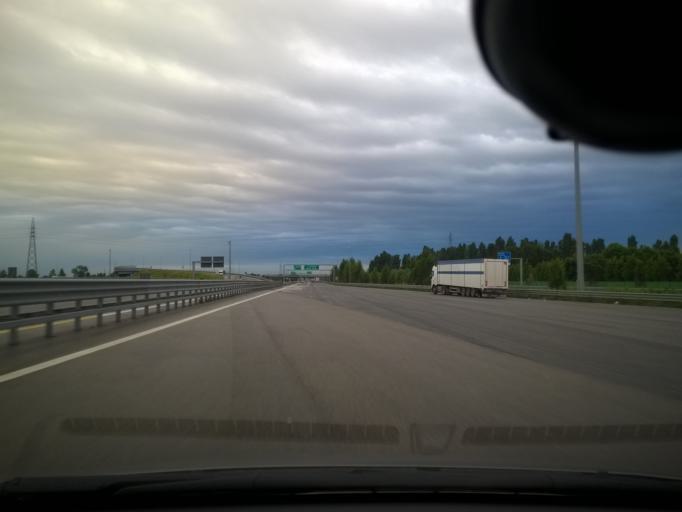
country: IT
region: Veneto
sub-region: Provincia di Venezia
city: San Liberale
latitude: 45.5703
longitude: 12.3381
